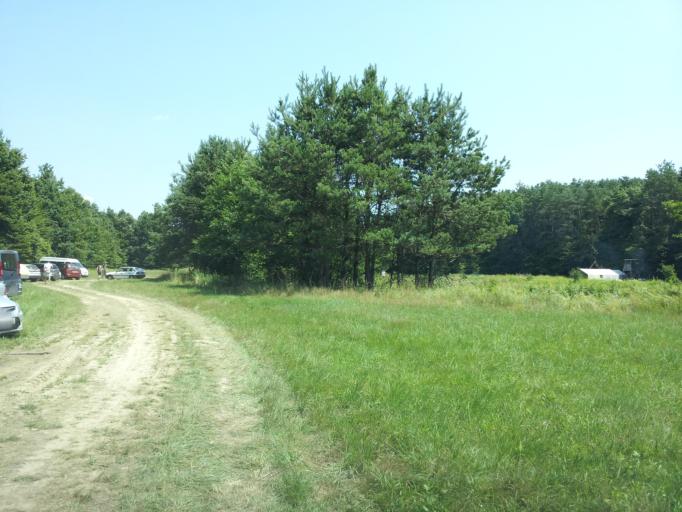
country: HU
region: Zala
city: Zalalovo
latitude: 46.7936
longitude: 16.4906
